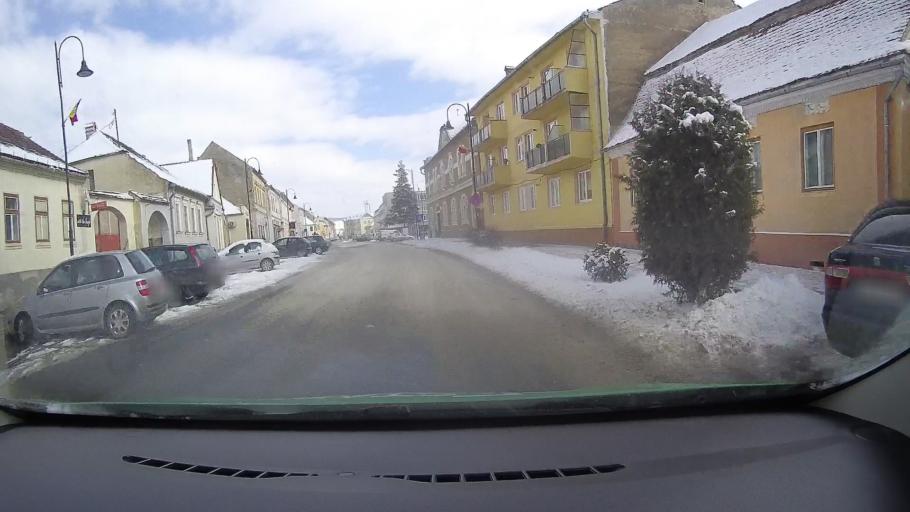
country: RO
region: Sibiu
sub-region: Oras Agnita
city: Agnita
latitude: 45.9756
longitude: 24.6210
